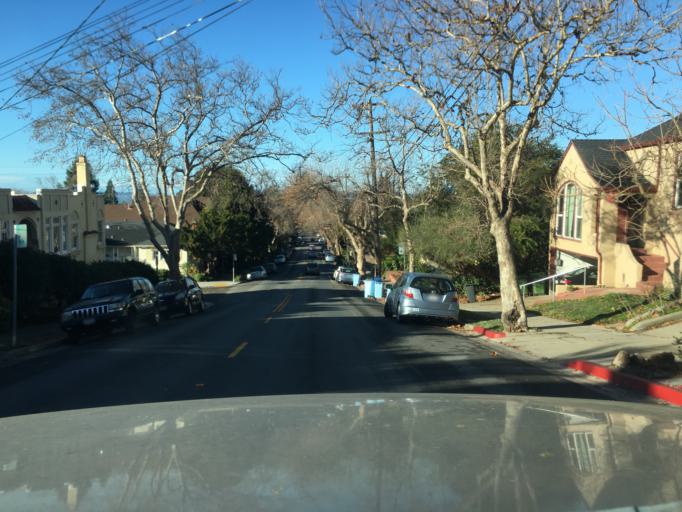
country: US
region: California
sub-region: Alameda County
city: Berkeley
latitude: 37.8793
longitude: -122.2625
